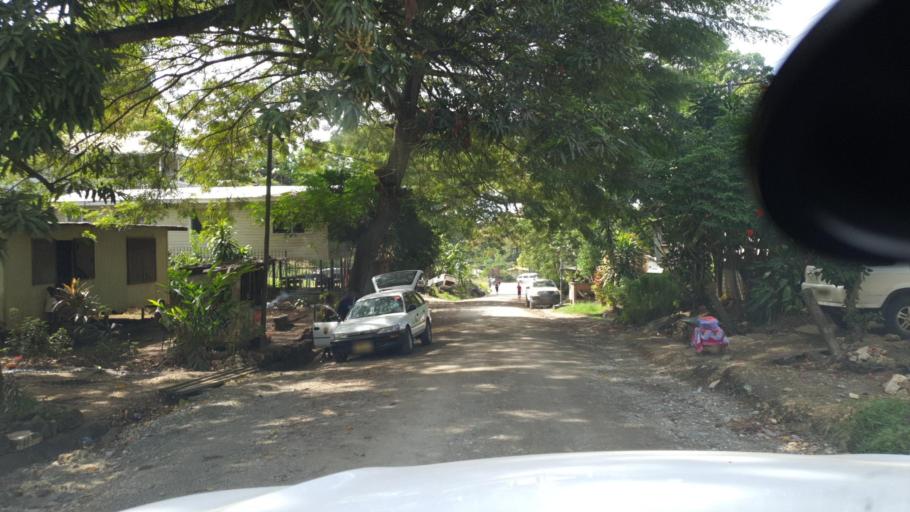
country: SB
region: Guadalcanal
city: Honiara
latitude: -9.4362
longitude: 159.9853
